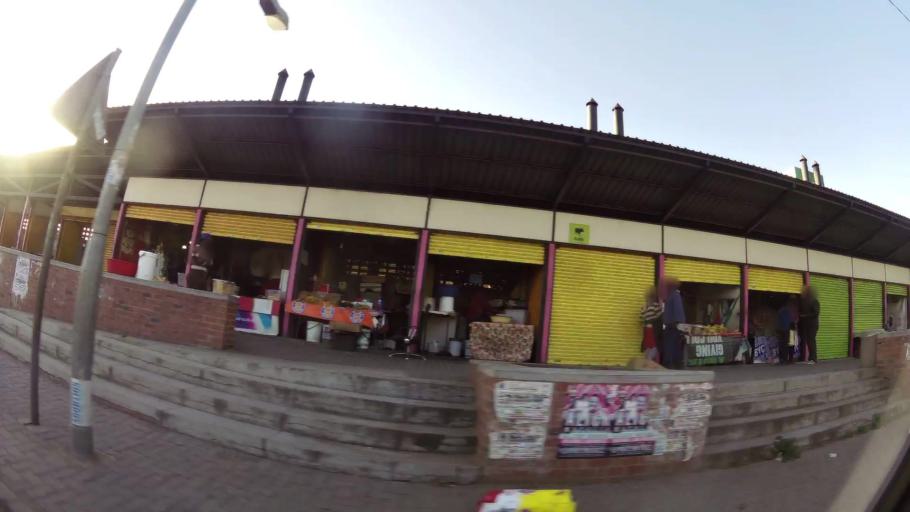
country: ZA
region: Gauteng
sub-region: City of Johannesburg Metropolitan Municipality
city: Diepsloot
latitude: -25.9229
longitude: 28.0206
